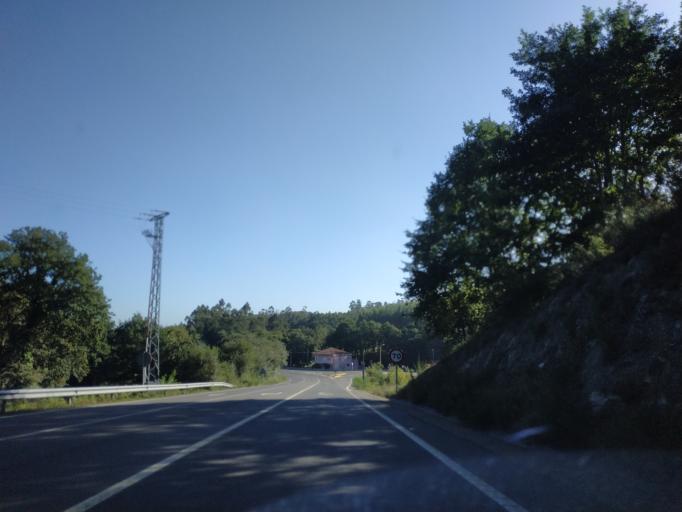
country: ES
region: Galicia
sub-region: Provincia da Coruna
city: Negreira
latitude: 42.9616
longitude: -8.7540
